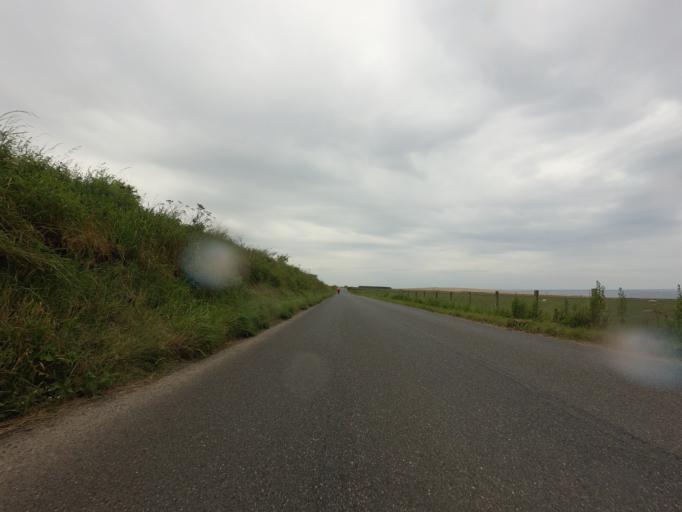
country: GB
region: Scotland
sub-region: Aberdeenshire
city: Whitehills
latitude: 57.6723
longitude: -2.6300
